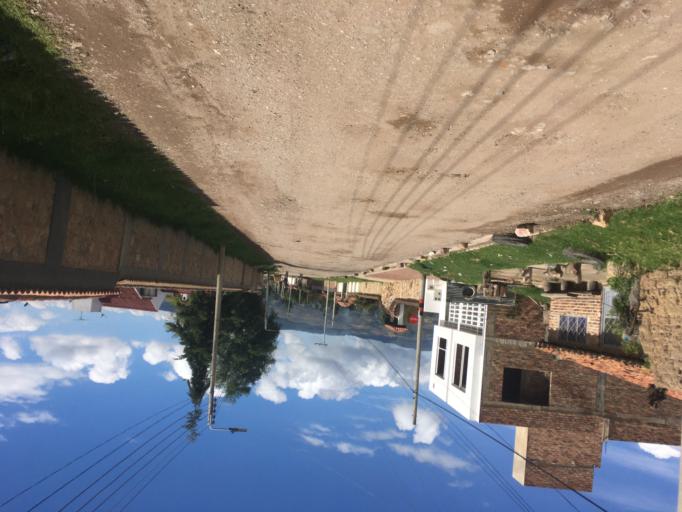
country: CO
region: Boyaca
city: Firavitoba
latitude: 5.6651
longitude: -72.9606
